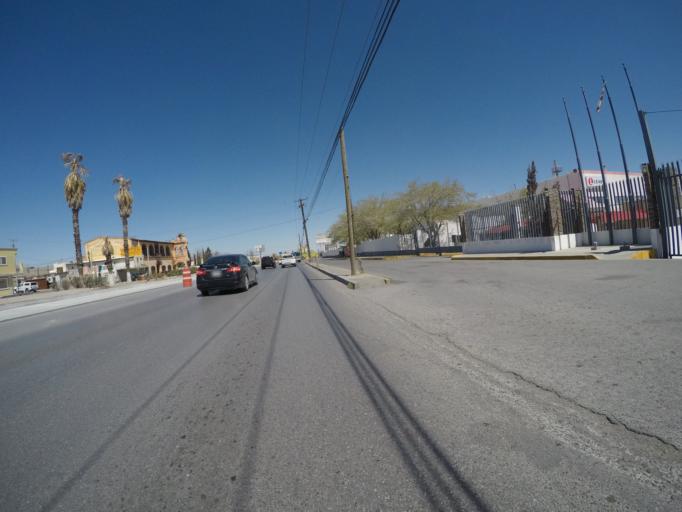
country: MX
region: Chihuahua
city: Ciudad Juarez
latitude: 31.6800
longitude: -106.4245
